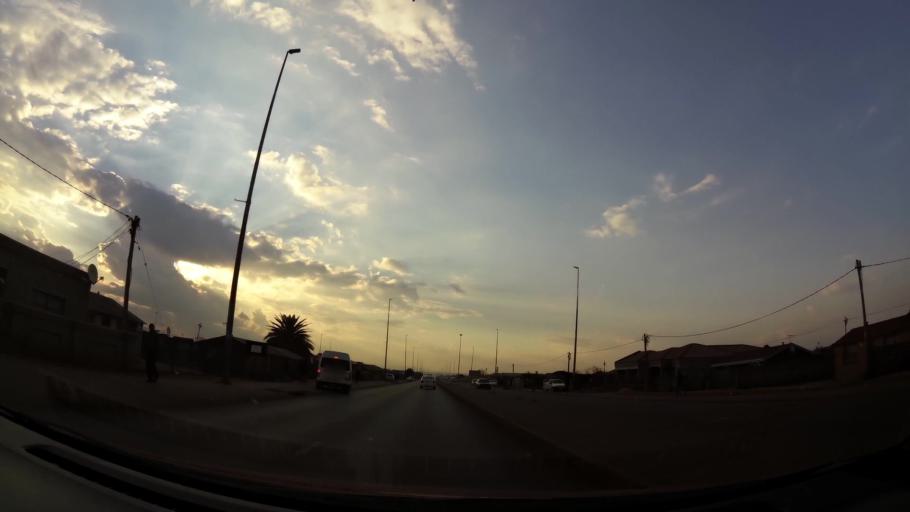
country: ZA
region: Gauteng
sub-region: City of Johannesburg Metropolitan Municipality
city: Orange Farm
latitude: -26.5679
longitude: 27.8360
